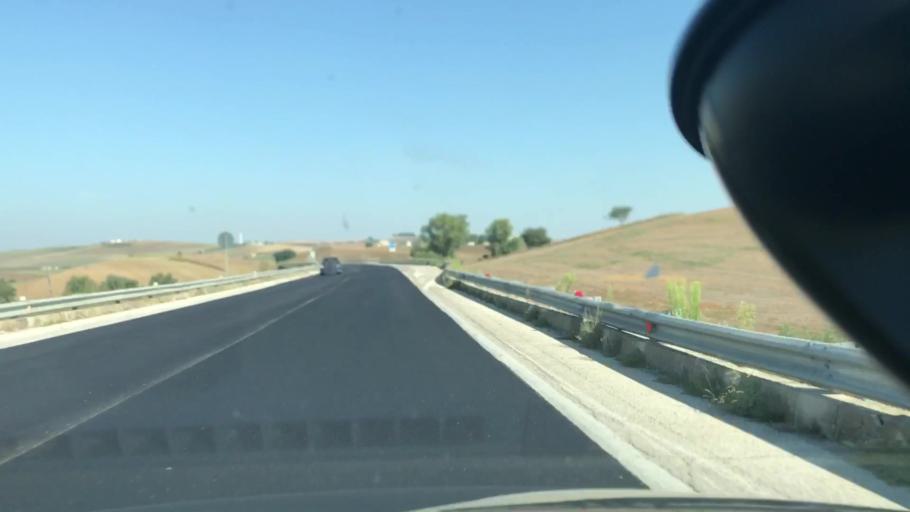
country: IT
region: Apulia
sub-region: Provincia di Barletta - Andria - Trani
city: Spinazzola
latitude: 40.9109
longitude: 16.1064
